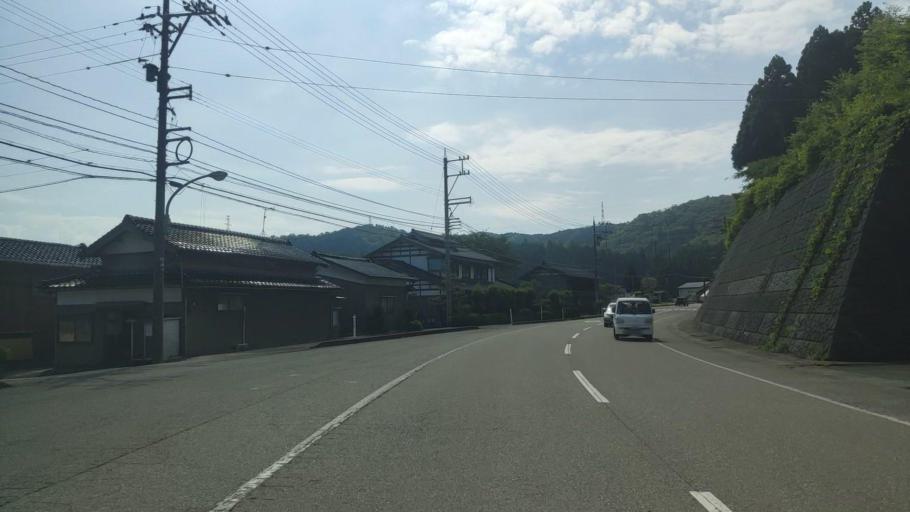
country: JP
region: Ishikawa
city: Komatsu
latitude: 36.3569
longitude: 136.5034
